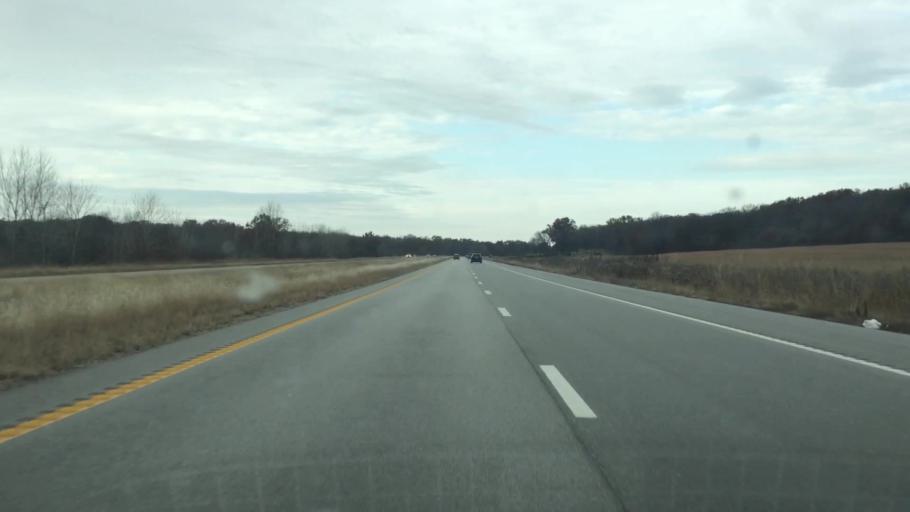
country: US
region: Missouri
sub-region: Henry County
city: Clinton
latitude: 38.2101
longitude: -93.7562
